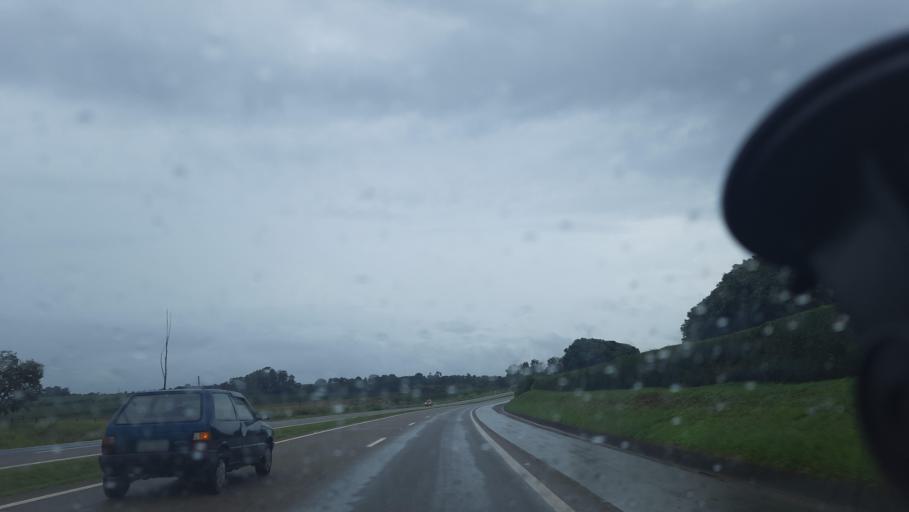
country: BR
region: Sao Paulo
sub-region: Casa Branca
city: Casa Branca
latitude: -21.7991
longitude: -47.0591
